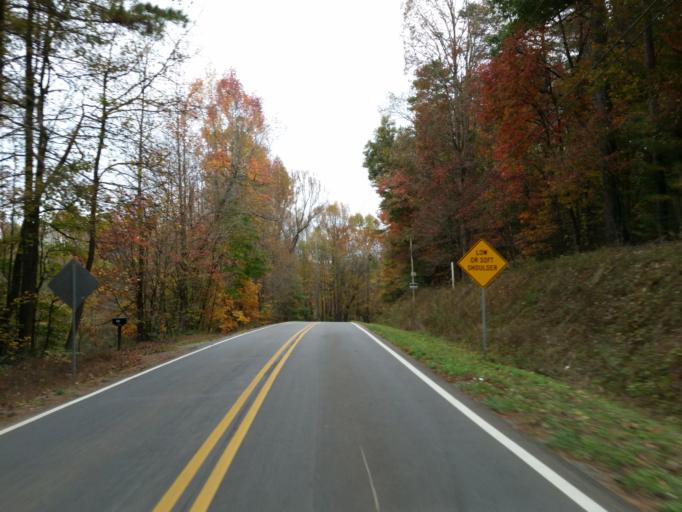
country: US
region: Georgia
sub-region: Gilmer County
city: Ellijay
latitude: 34.6574
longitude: -84.3804
